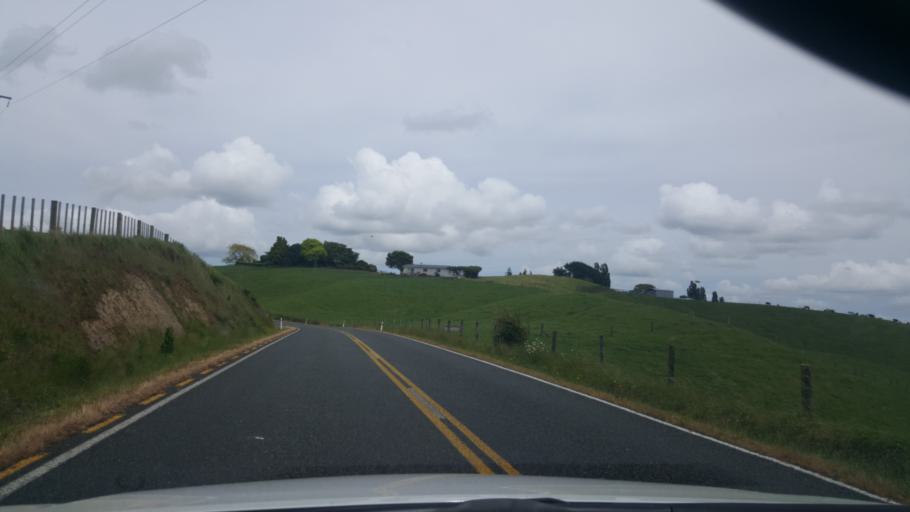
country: NZ
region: Waikato
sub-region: Matamata-Piako District
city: Matamata
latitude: -37.8751
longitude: 175.6854
